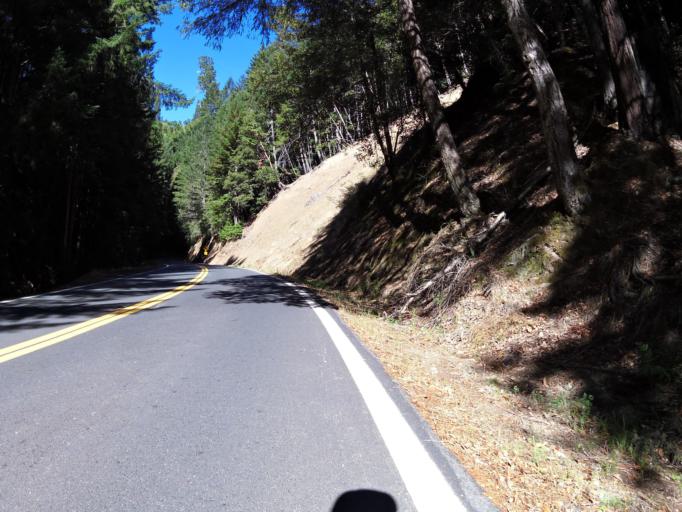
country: US
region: California
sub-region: Humboldt County
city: Redway
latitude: 39.8520
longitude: -123.7348
